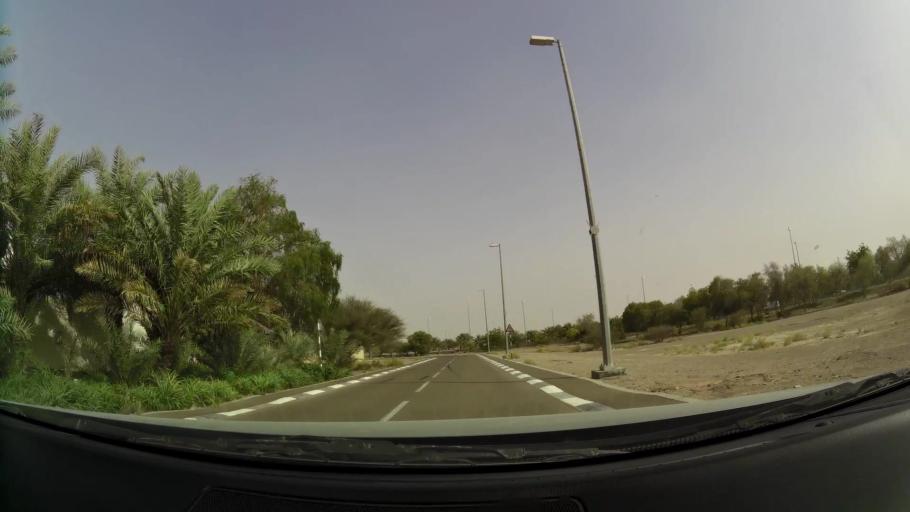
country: AE
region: Abu Dhabi
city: Al Ain
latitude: 24.1782
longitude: 55.6040
